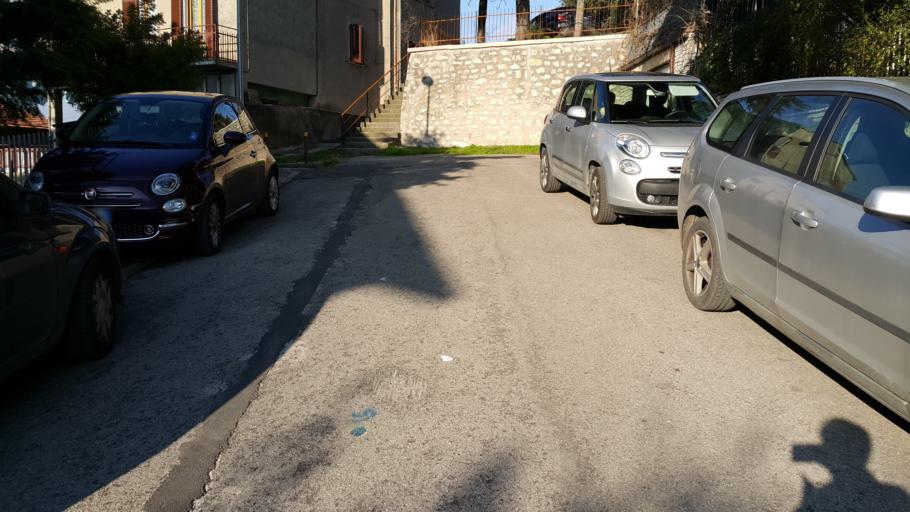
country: IT
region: Umbria
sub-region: Provincia di Perugia
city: Perugia
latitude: 43.0892
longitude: 12.3696
